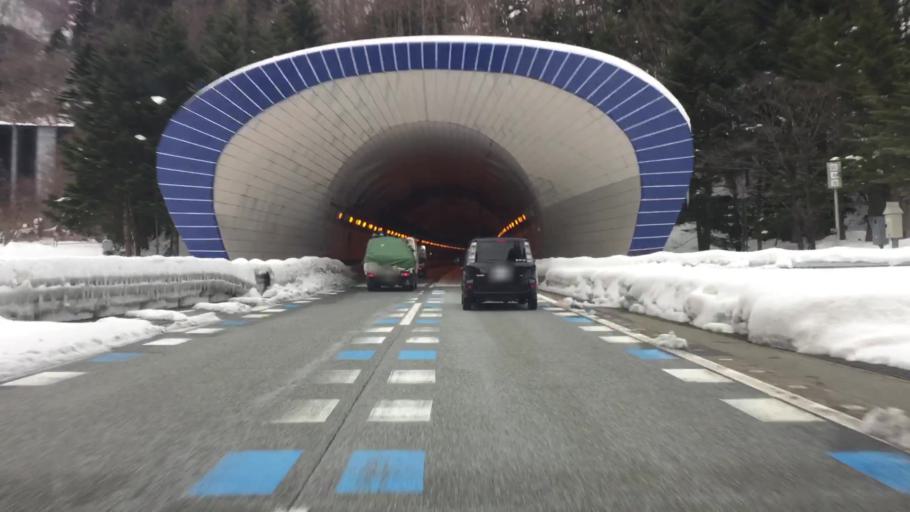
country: JP
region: Gunma
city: Numata
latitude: 36.7801
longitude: 138.9391
